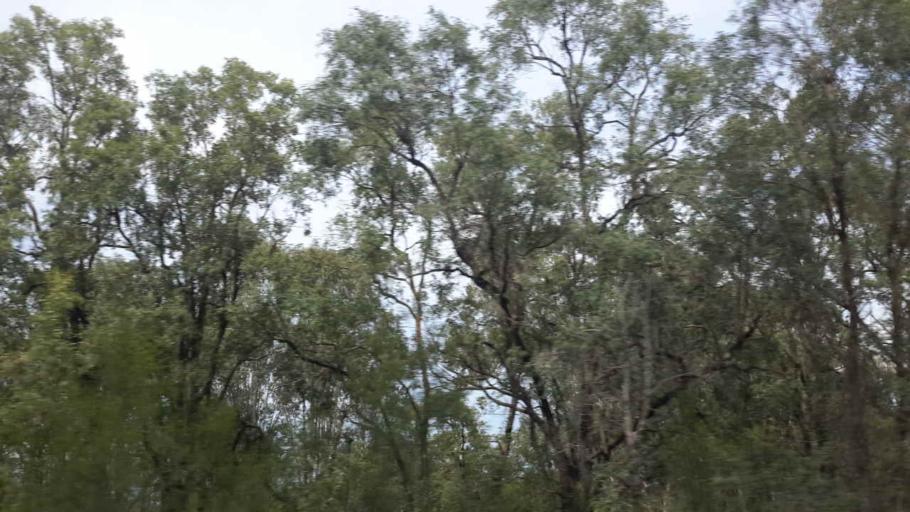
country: AU
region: New South Wales
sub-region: Hawkesbury
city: South Windsor
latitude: -33.6364
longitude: 150.7812
